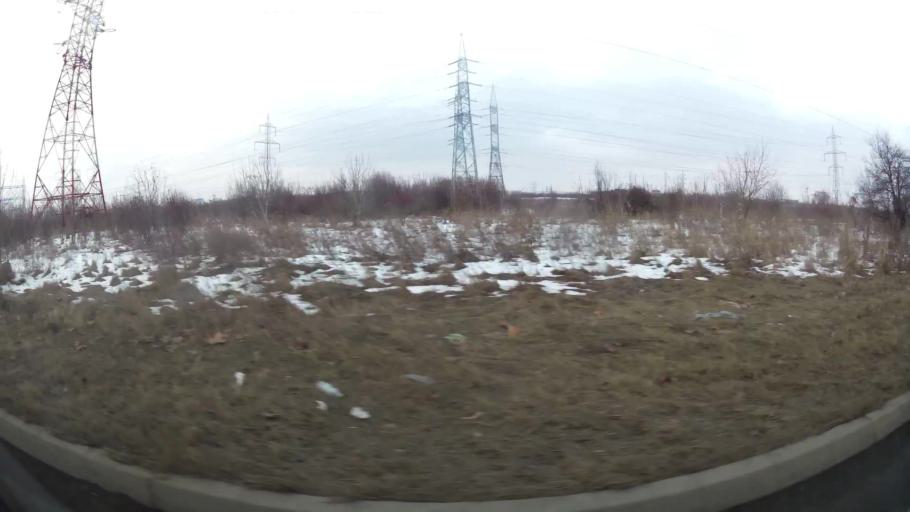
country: RO
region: Ilfov
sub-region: Comuna Popesti-Leordeni
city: Popesti-Leordeni
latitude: 44.3944
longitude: 26.1846
